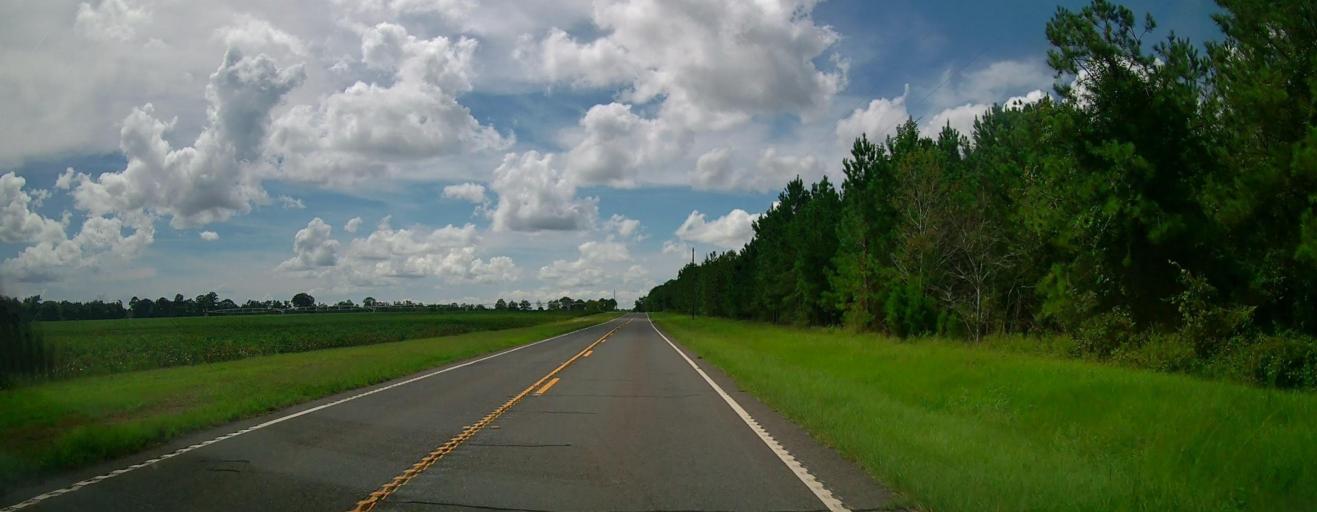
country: US
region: Georgia
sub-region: Macon County
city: Marshallville
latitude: 32.4335
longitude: -84.0587
